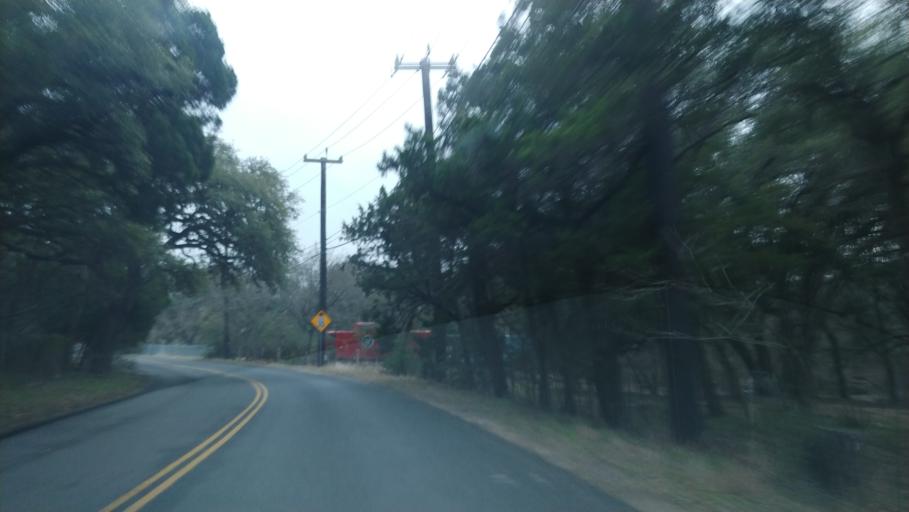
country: US
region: Texas
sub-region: Bexar County
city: Cross Mountain
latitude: 29.6299
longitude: -98.6825
